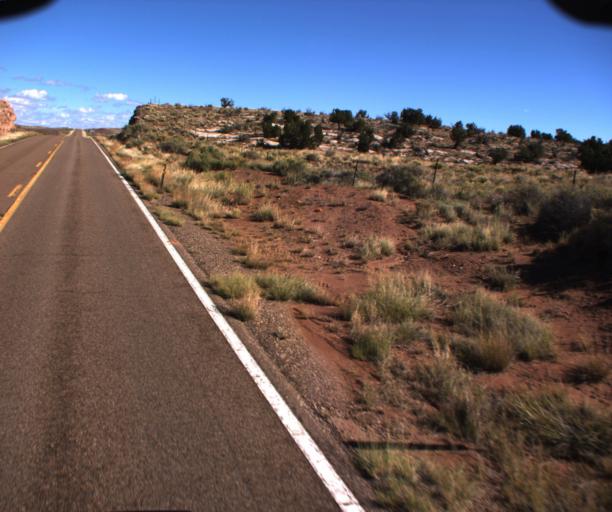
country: US
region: Arizona
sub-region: Apache County
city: Saint Johns
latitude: 34.6501
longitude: -109.2996
